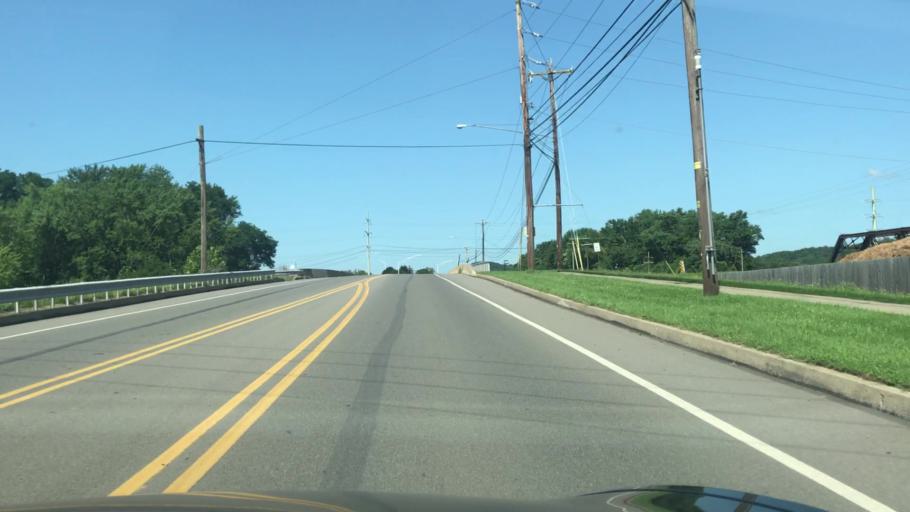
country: US
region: Pennsylvania
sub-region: Lycoming County
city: Duboistown
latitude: 41.2369
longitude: -77.0411
